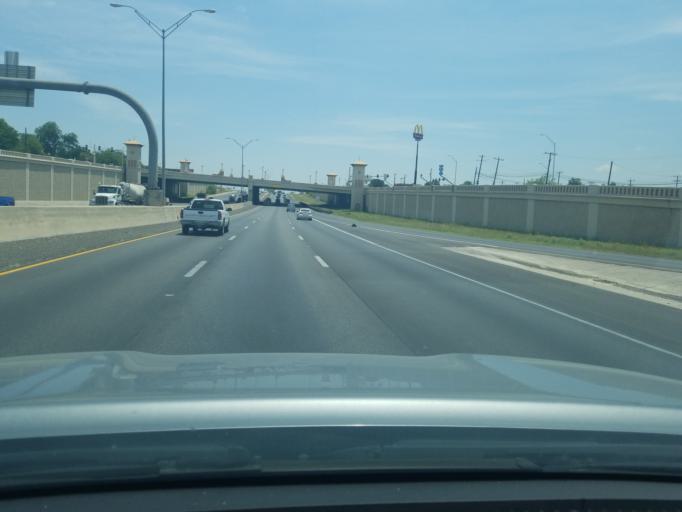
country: US
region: Texas
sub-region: Bexar County
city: Terrell Hills
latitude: 29.4390
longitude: -98.4526
